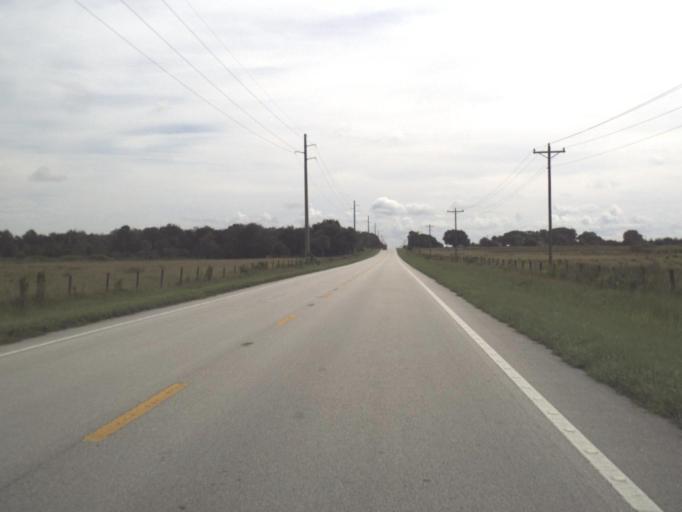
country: US
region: Florida
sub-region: Highlands County
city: Placid Lakes
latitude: 27.2088
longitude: -81.4180
